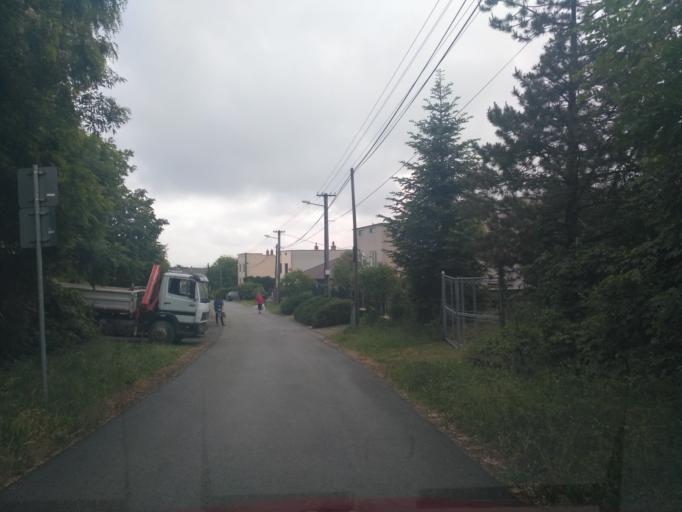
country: SK
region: Kosicky
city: Moldava nad Bodvou
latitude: 48.6909
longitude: 21.0743
